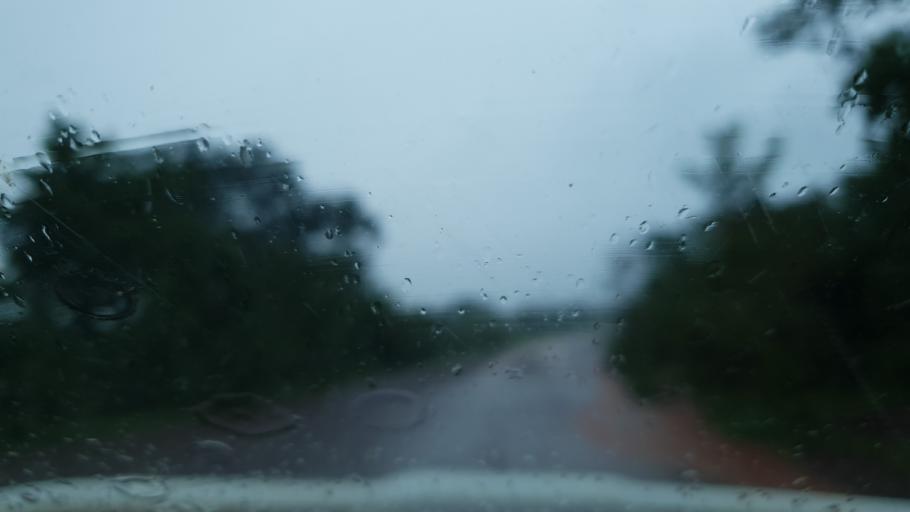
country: ML
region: Sikasso
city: Kolondieba
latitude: 11.6161
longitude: -6.6774
